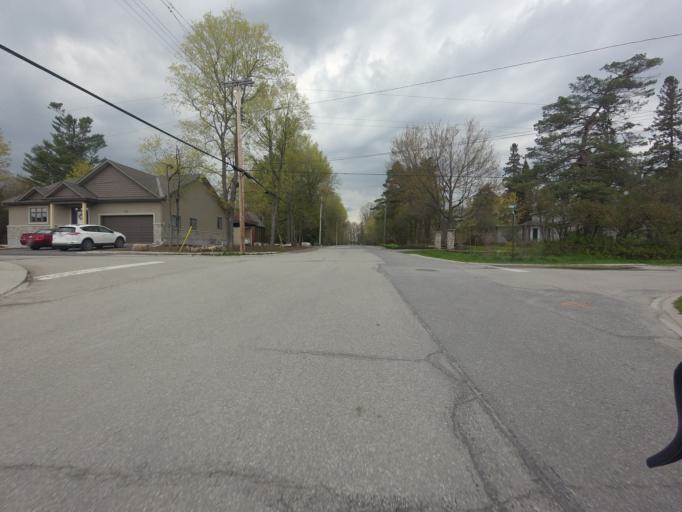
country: CA
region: Ontario
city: Carleton Place
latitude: 45.2259
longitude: -76.2040
